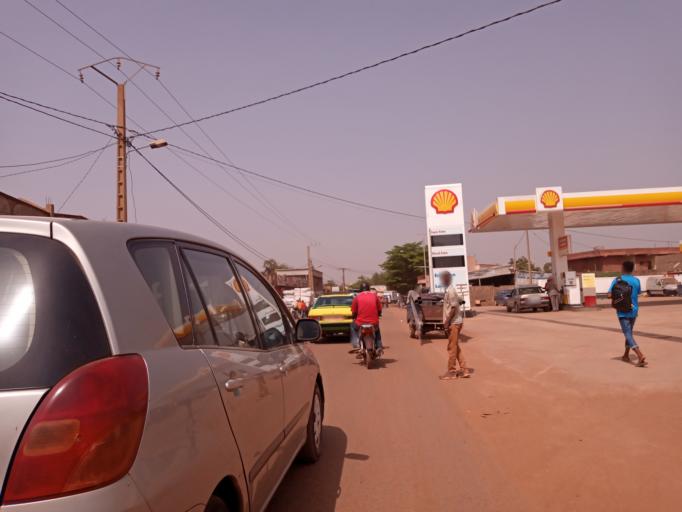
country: ML
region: Bamako
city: Bamako
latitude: 12.5884
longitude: -7.9770
